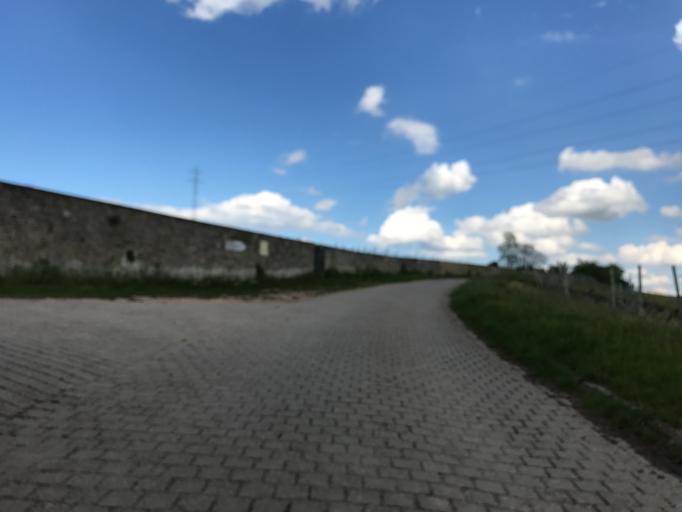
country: DE
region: Rheinland-Pfalz
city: Stadecken-Elsheim
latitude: 49.9251
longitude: 8.1242
